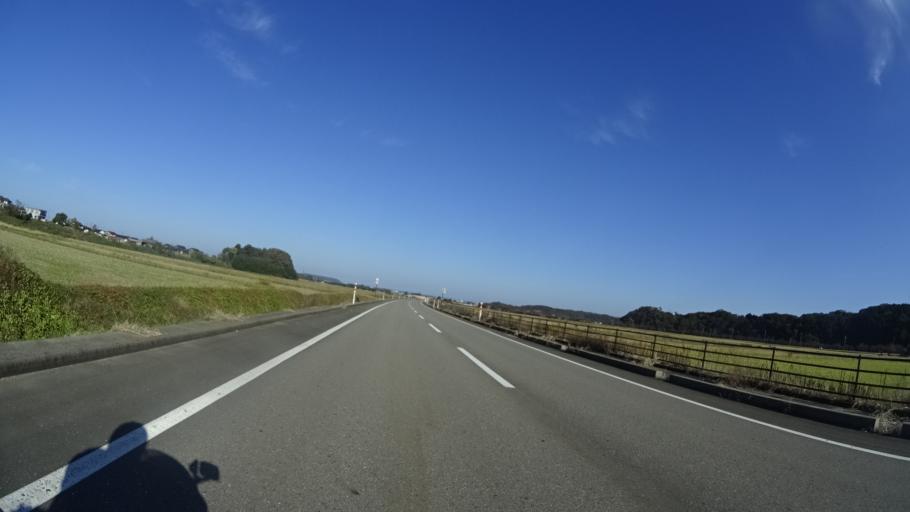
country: JP
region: Ishikawa
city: Komatsu
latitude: 36.2914
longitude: 136.3893
